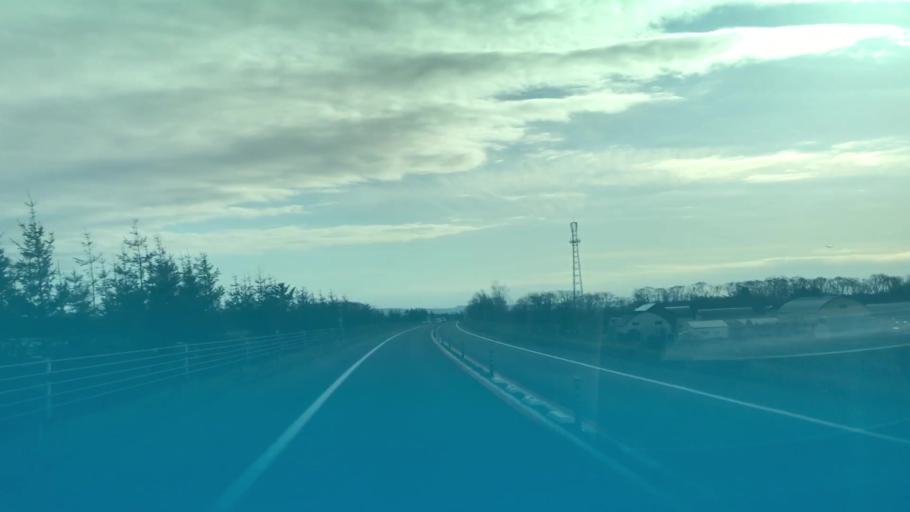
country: JP
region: Hokkaido
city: Chitose
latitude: 42.8841
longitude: 141.6341
